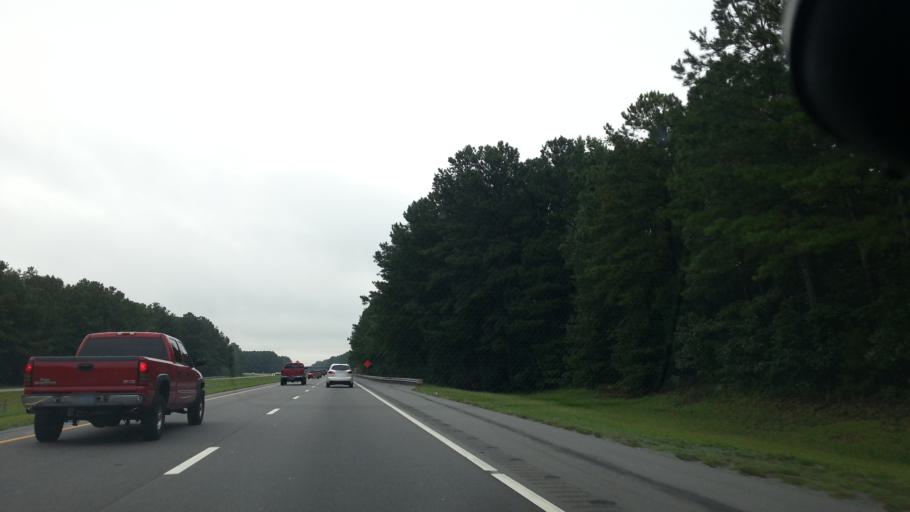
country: US
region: North Carolina
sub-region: Cumberland County
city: Fort Bragg
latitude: 35.0899
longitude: -78.9665
